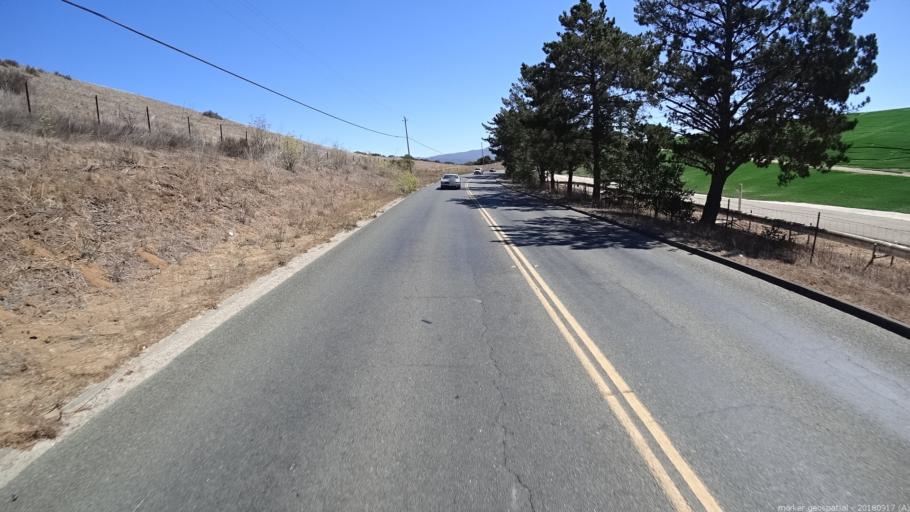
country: US
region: California
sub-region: Monterey County
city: Prunedale
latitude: 36.8059
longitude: -121.6174
